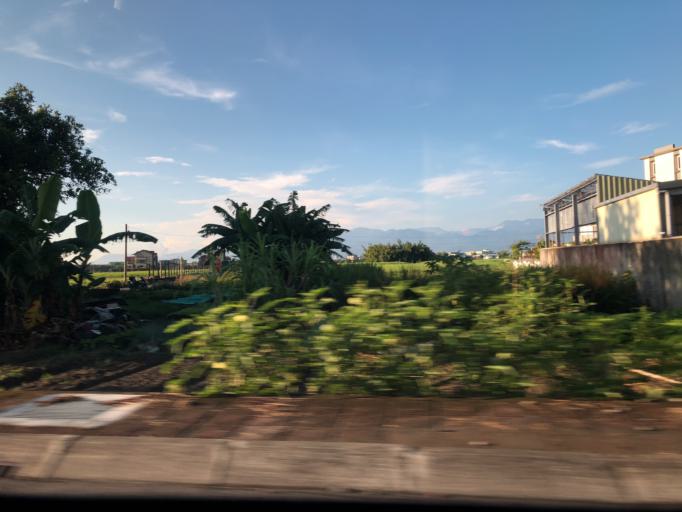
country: TW
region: Taiwan
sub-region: Yilan
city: Yilan
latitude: 24.7492
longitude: 121.7779
